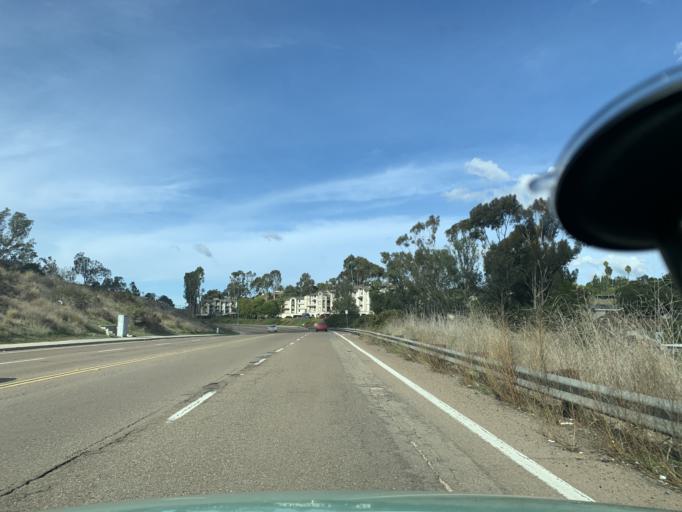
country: US
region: California
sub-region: San Diego County
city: San Diego
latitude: 32.8078
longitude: -117.1763
